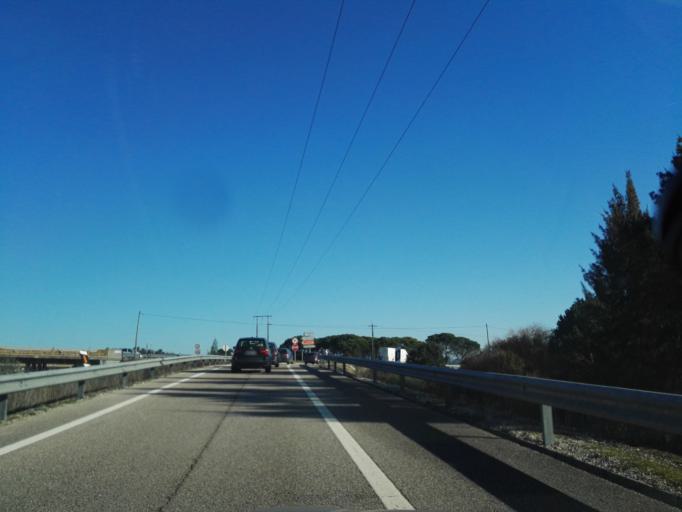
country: PT
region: Santarem
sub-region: Constancia
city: Constancia
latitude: 39.4843
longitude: -8.3273
